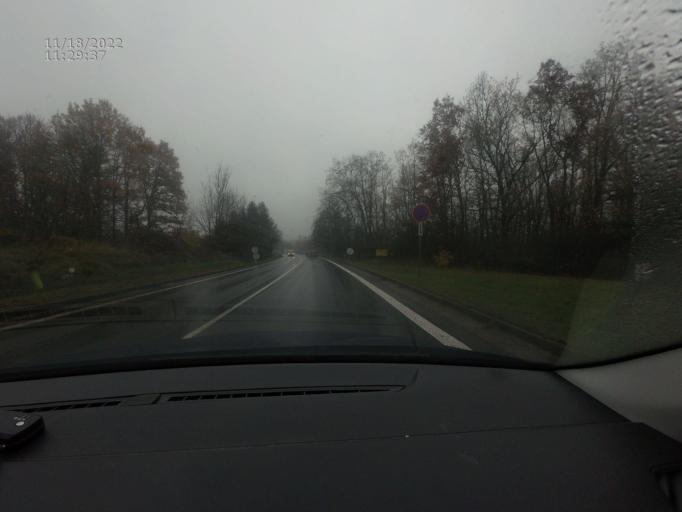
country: CZ
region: Plzensky
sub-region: Okres Rokycany
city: Rokycany
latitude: 49.7487
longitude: 13.5767
